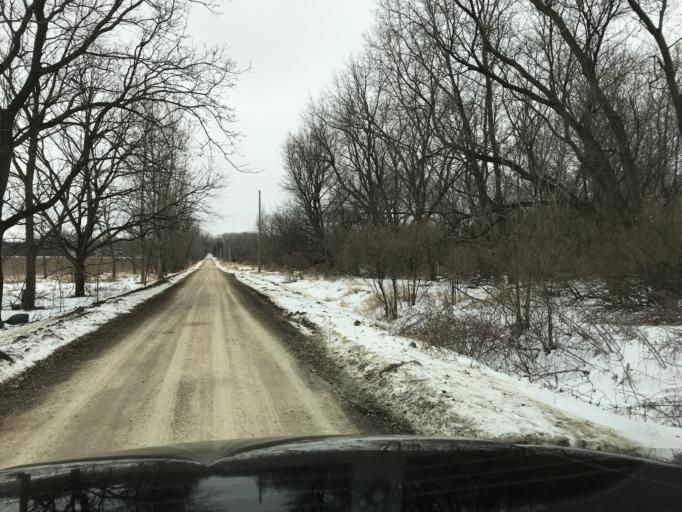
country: US
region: Wisconsin
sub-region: Dane County
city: McFarland
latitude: 43.0738
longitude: -89.2666
